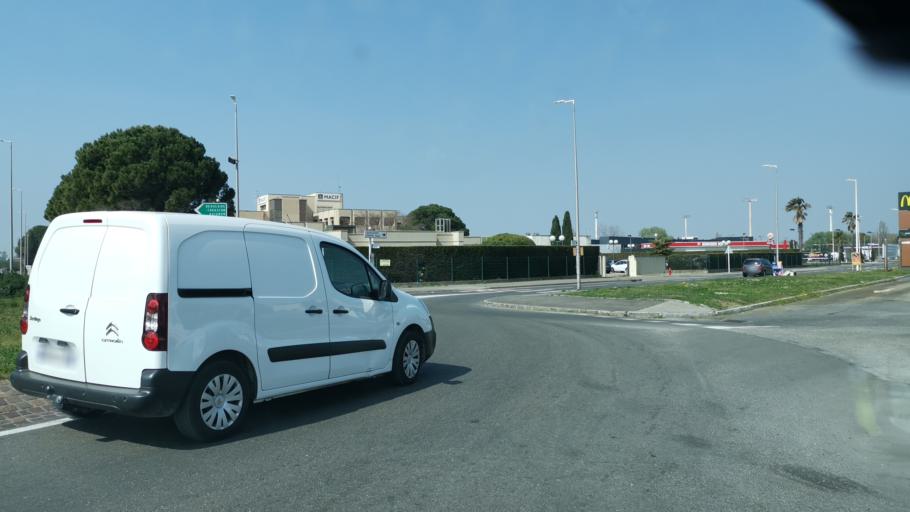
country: FR
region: Provence-Alpes-Cote d'Azur
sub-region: Departement des Bouches-du-Rhone
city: Arles
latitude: 43.6659
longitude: 4.6363
